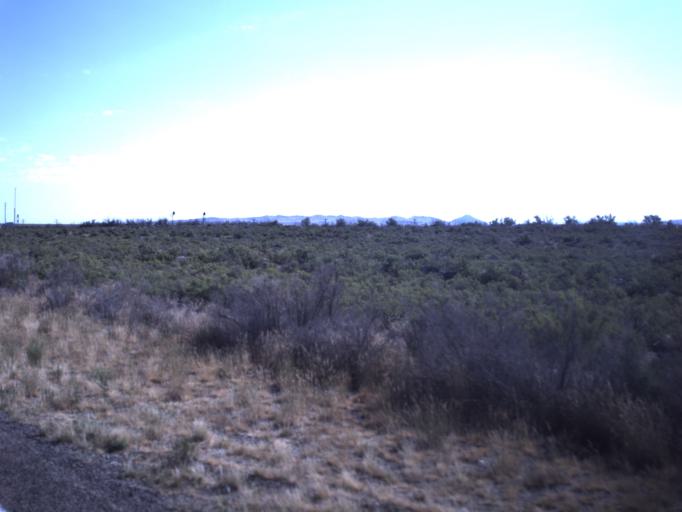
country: US
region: Utah
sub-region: Beaver County
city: Milford
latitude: 38.5971
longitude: -112.9876
